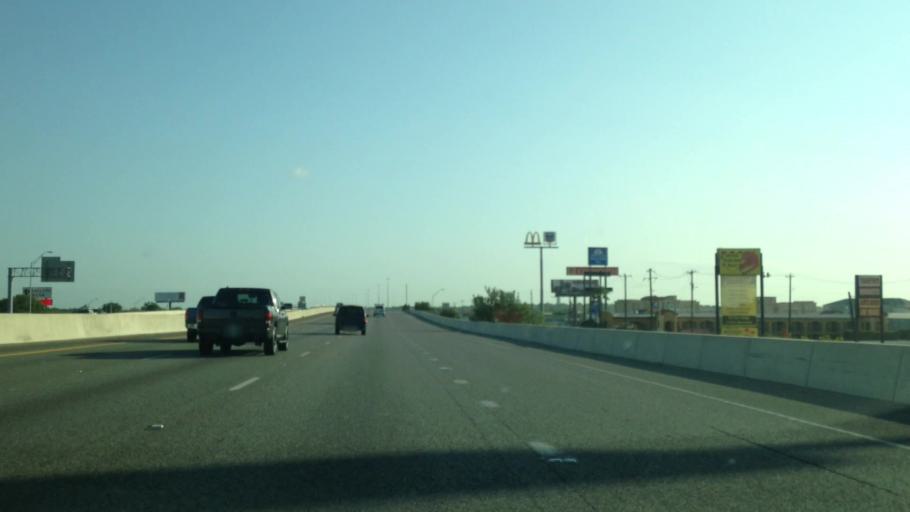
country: US
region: Texas
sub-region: Hays County
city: Buda
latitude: 30.0863
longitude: -97.8197
